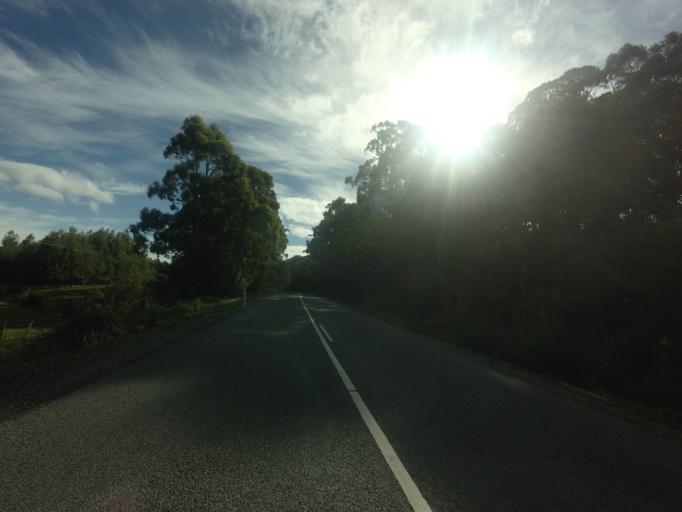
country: AU
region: Tasmania
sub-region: Clarence
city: Sandford
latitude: -43.1371
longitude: 147.8133
